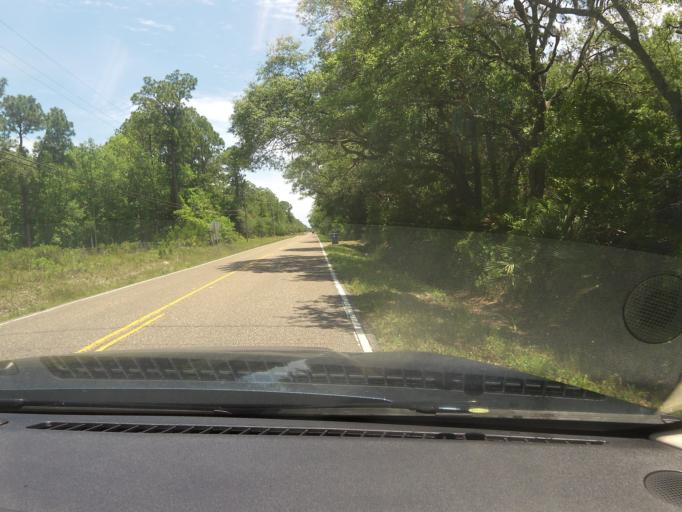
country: US
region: Florida
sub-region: Duval County
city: Atlantic Beach
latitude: 30.4576
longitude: -81.5163
